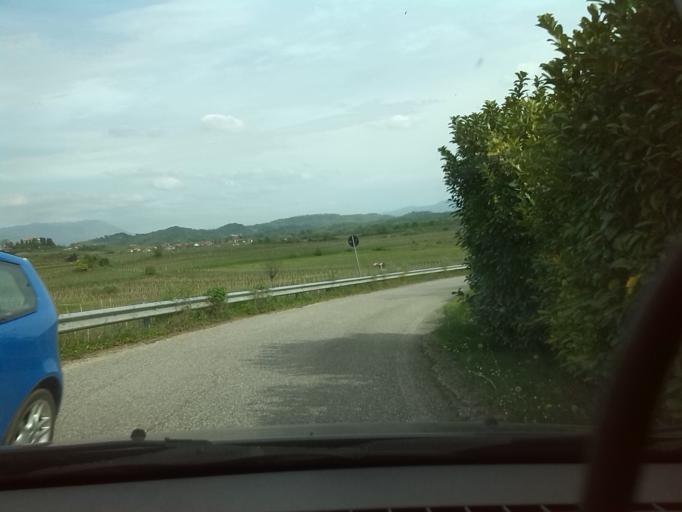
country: SI
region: Brda
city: Dobrovo
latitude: 45.9736
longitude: 13.5165
